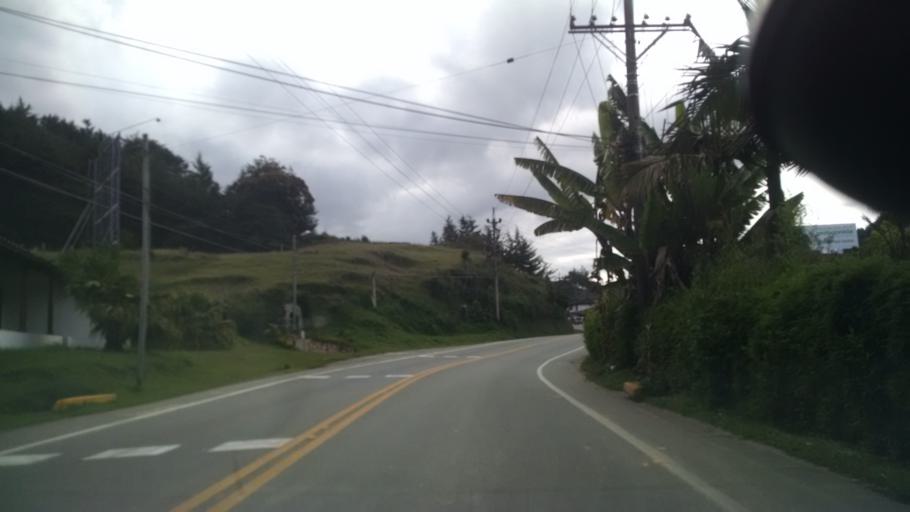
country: CO
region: Antioquia
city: El Retiro
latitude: 6.0912
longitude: -75.4813
